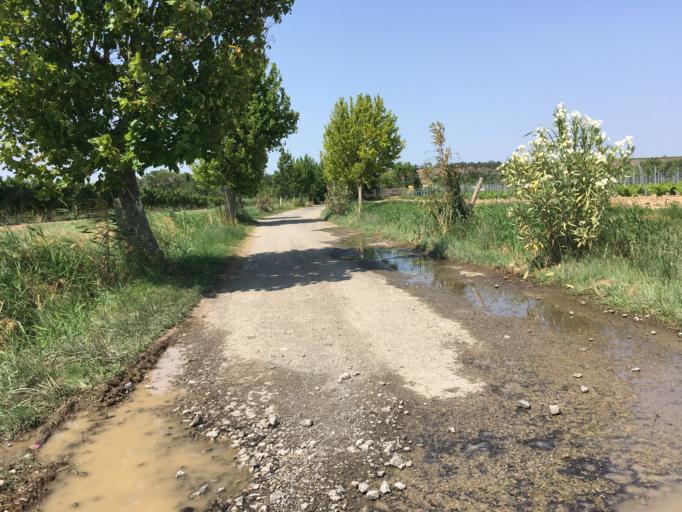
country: FR
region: Languedoc-Roussillon
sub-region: Departement de l'Aude
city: Puicheric
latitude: 43.2280
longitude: 2.6224
